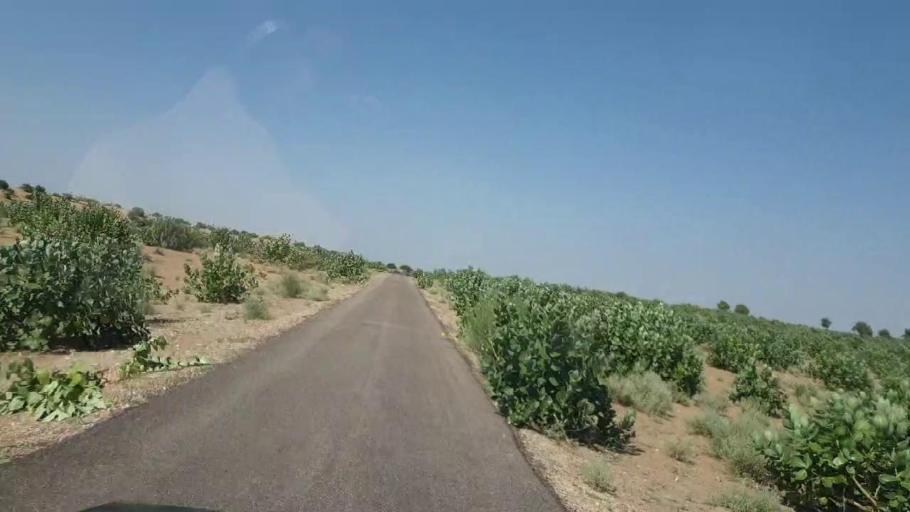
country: PK
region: Sindh
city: Chor
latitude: 25.6401
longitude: 70.3188
